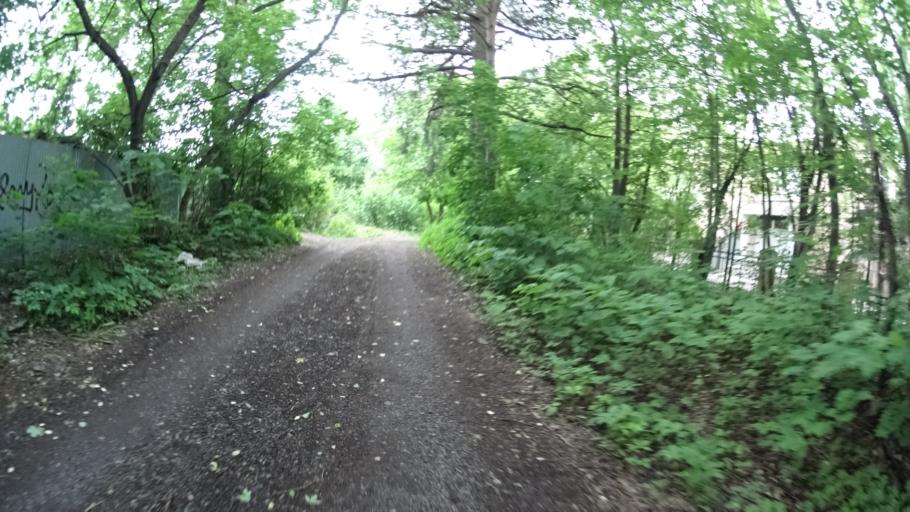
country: RU
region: Moskovskaya
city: Sofrino
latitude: 56.1323
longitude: 37.9346
